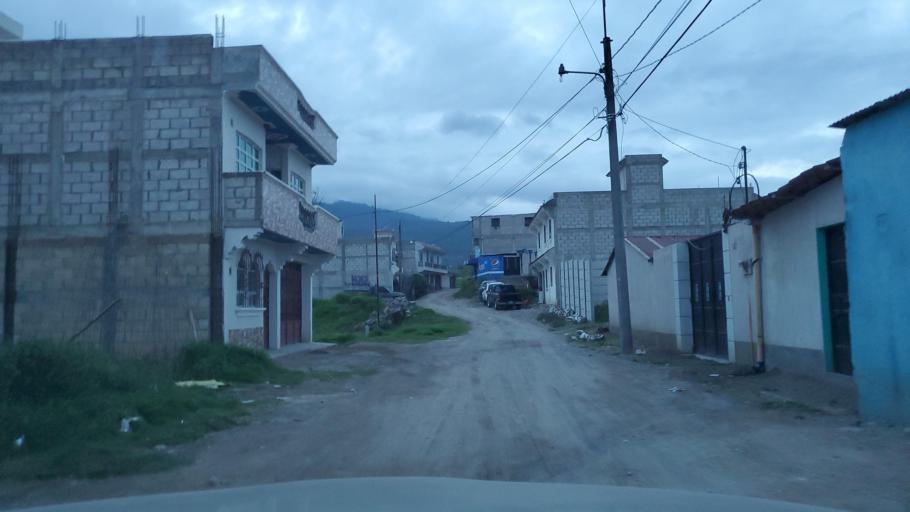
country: GT
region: Quetzaltenango
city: Quetzaltenango
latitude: 14.8257
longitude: -91.5370
